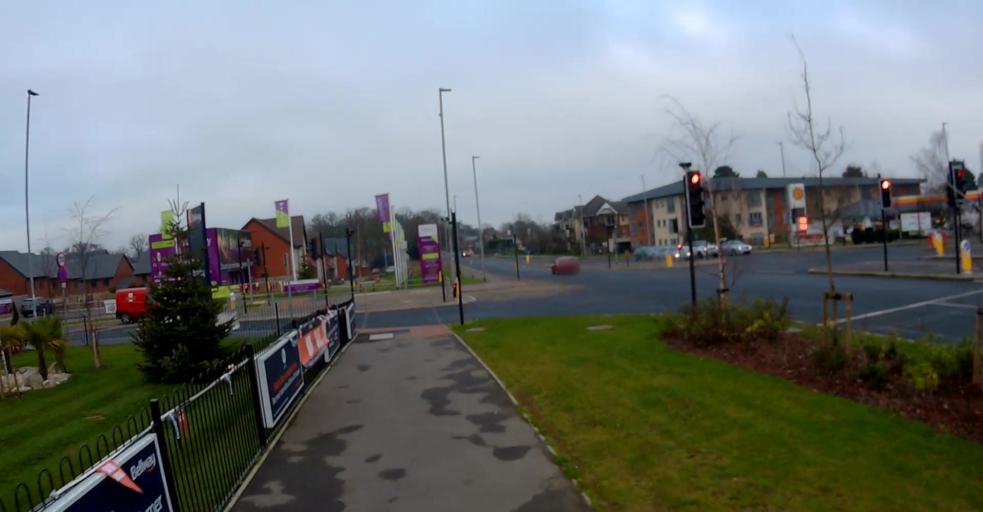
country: GB
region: England
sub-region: Bracknell Forest
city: Binfield
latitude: 51.4161
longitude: -0.7909
